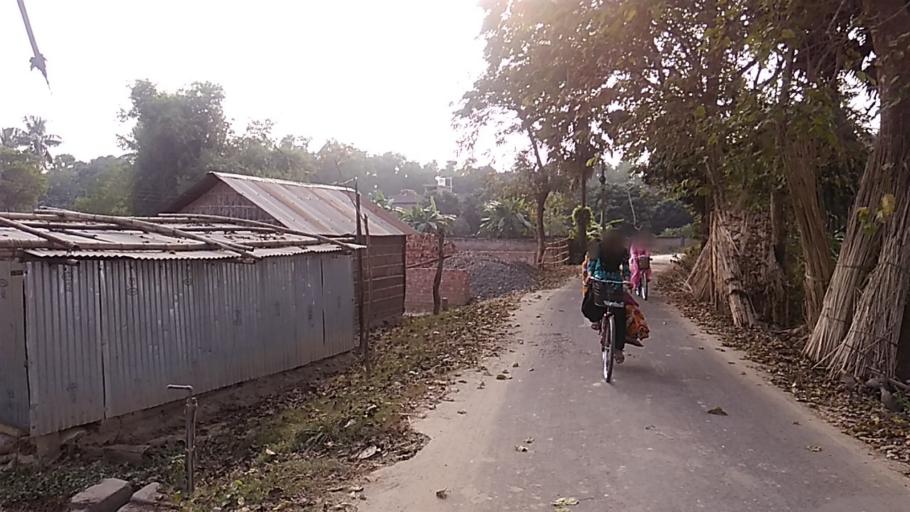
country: IN
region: West Bengal
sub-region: Nadia
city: Navadwip
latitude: 23.4264
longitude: 88.3995
